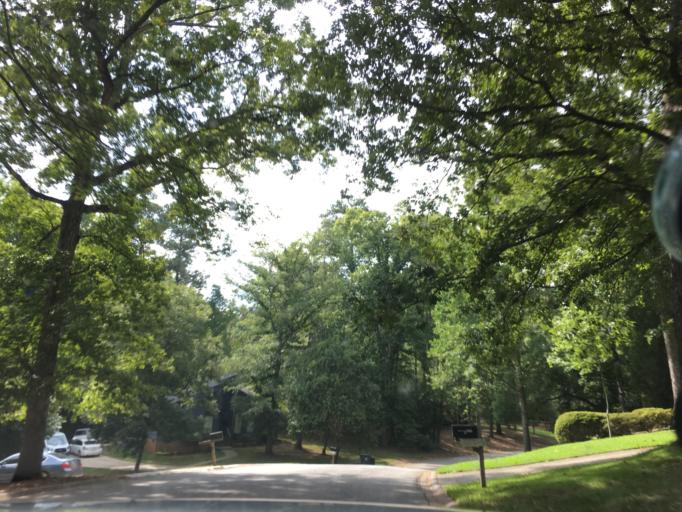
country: US
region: South Carolina
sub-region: Lexington County
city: Irmo
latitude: 34.0627
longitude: -81.1862
